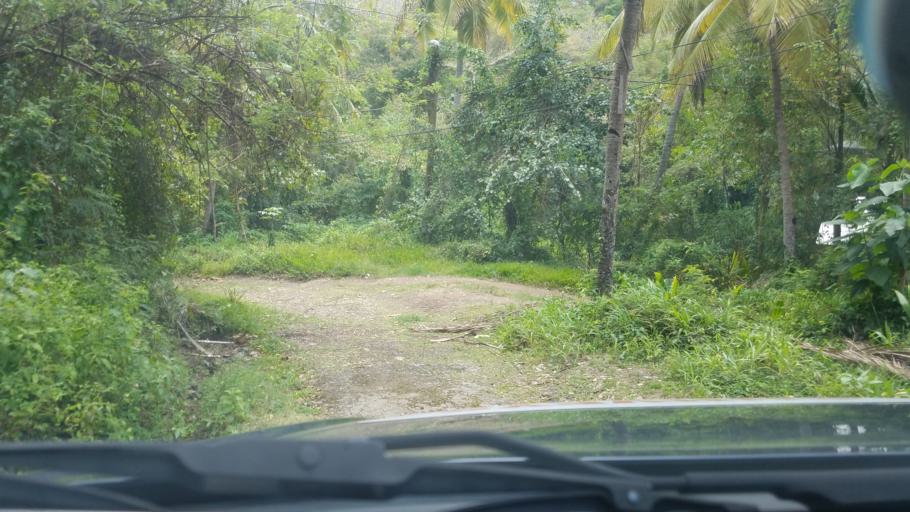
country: LC
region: Gros-Islet
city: Gros Islet
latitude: 14.0631
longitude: -60.9529
